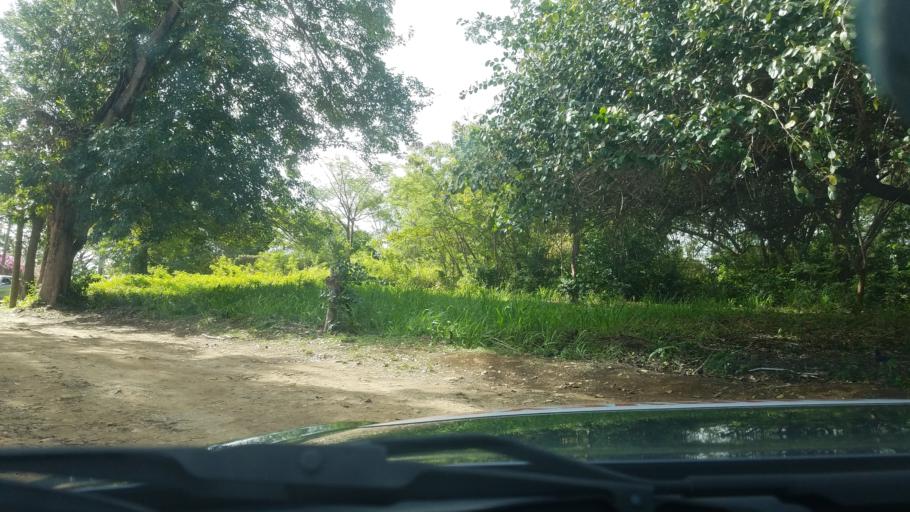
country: LC
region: Gros-Islet
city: Gros Islet
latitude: 14.0712
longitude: -60.9577
